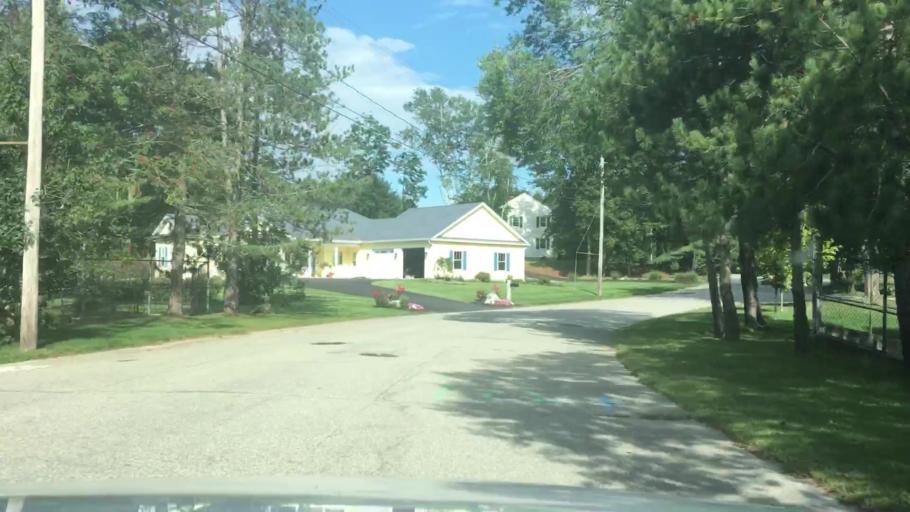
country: US
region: Maine
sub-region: Androscoggin County
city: Lewiston
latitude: 44.1153
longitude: -70.1993
